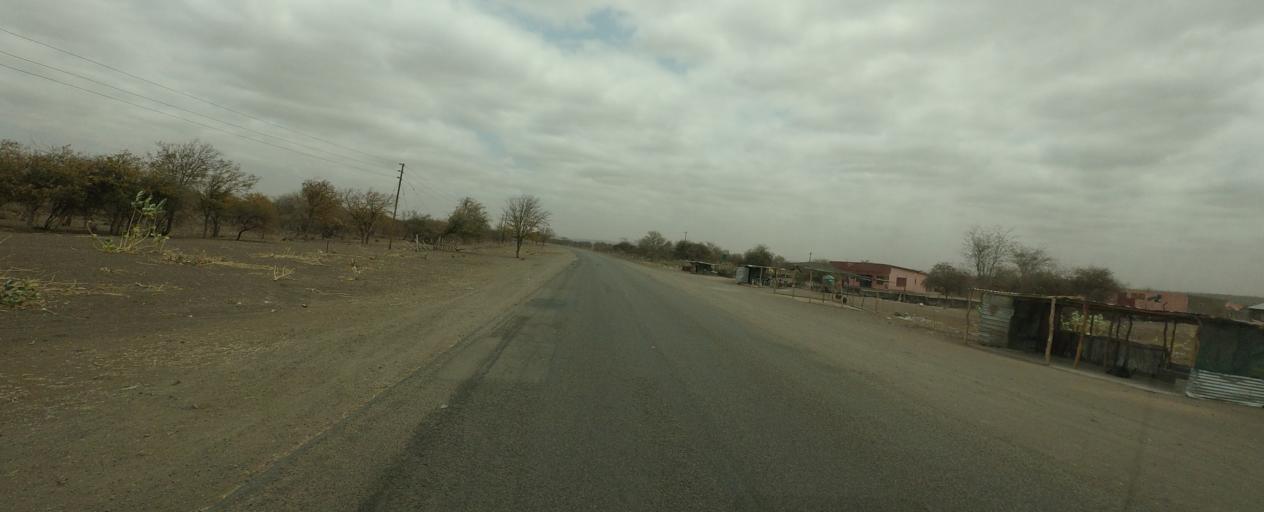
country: ZA
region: Limpopo
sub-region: Vhembe District Municipality
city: Mutale
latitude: -22.4012
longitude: 30.5855
